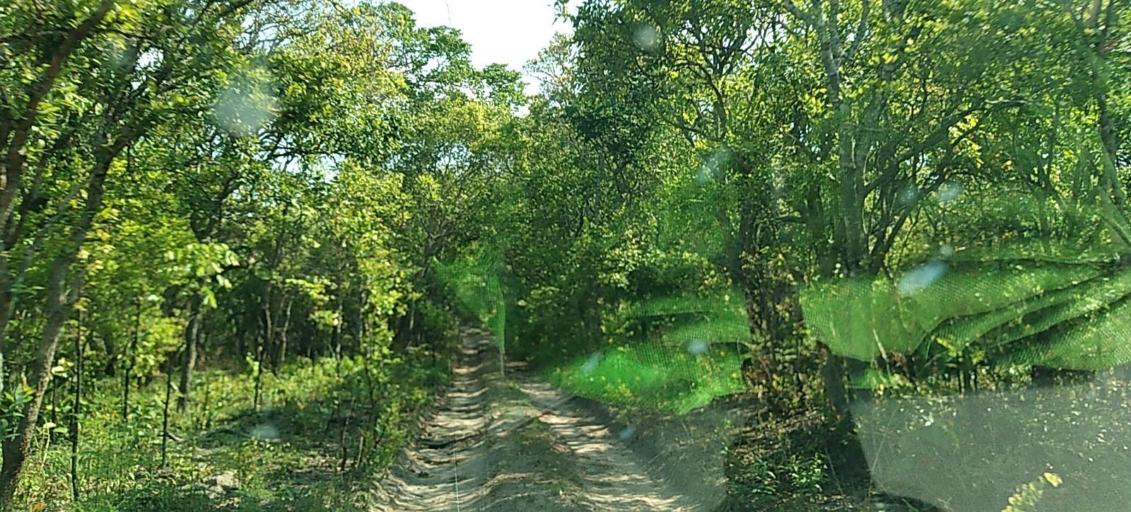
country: ZM
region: North-Western
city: Mwinilunga
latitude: -11.2791
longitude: 24.9264
